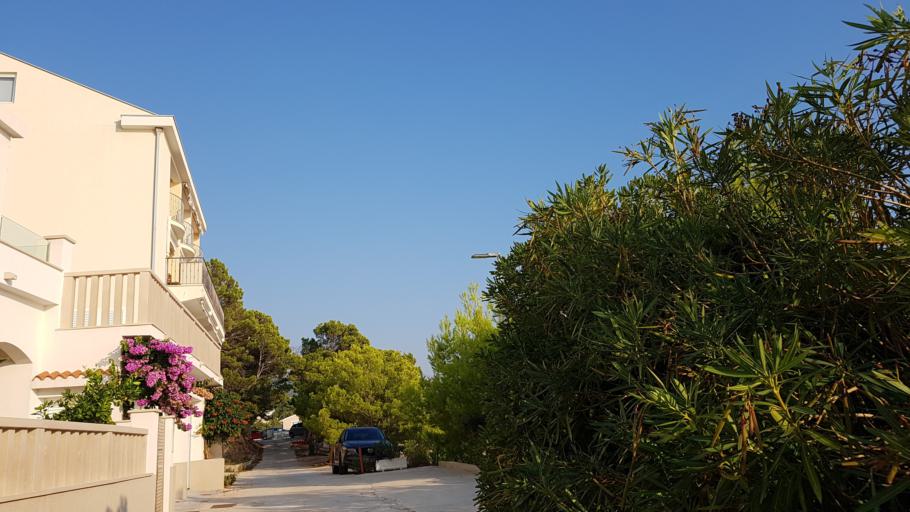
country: HR
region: Splitsko-Dalmatinska
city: Donja Brela
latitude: 43.3875
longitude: 16.8997
